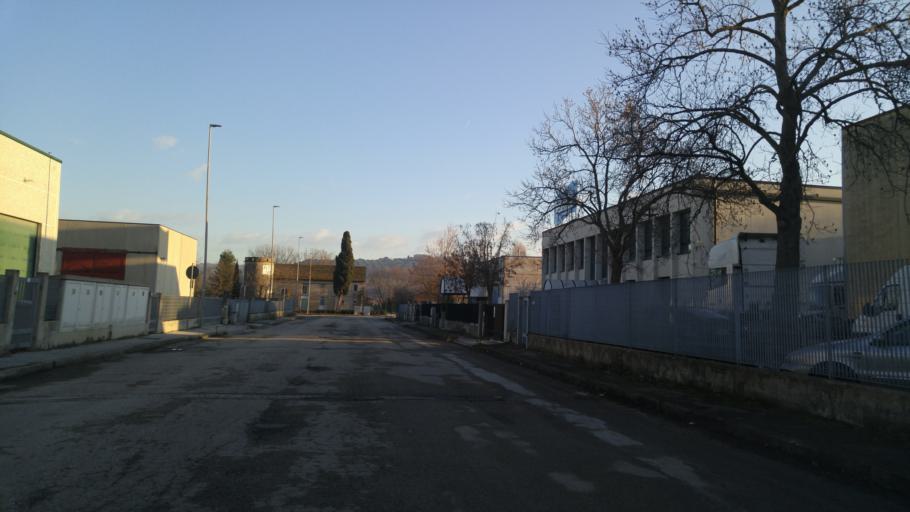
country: IT
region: The Marches
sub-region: Provincia di Ancona
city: Monterado
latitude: 43.7096
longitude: 13.0772
